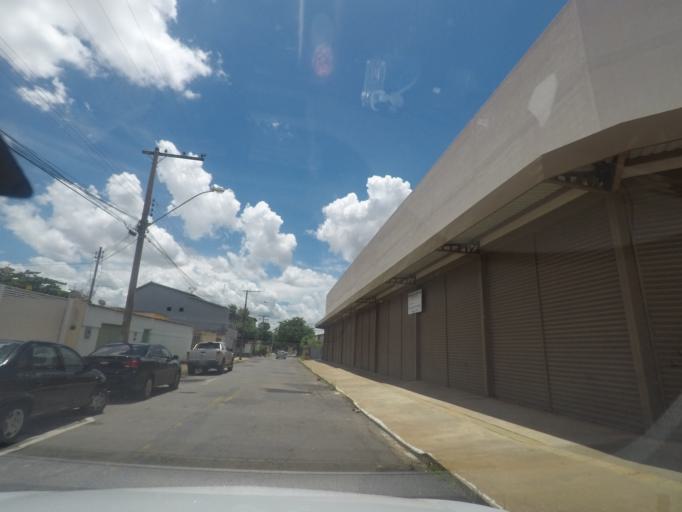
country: BR
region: Goias
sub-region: Goiania
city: Goiania
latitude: -16.6652
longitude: -49.2873
